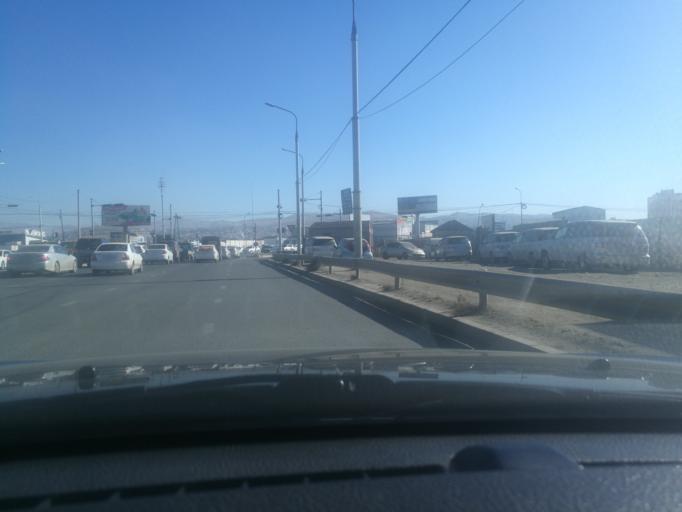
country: MN
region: Ulaanbaatar
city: Ulaanbaatar
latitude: 47.9396
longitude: 106.9138
